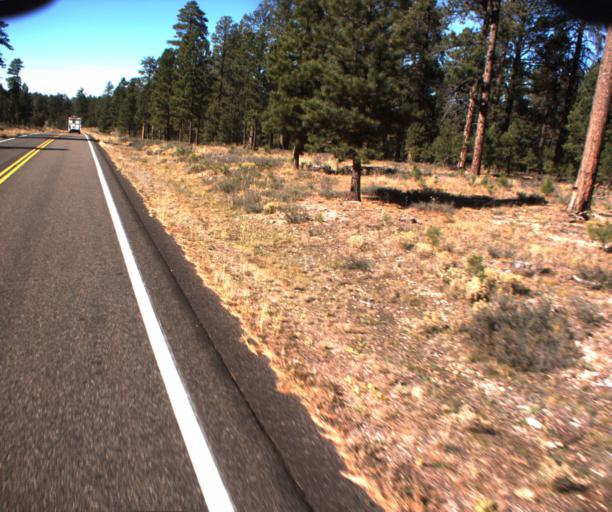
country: US
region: Arizona
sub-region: Coconino County
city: Fredonia
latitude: 36.6679
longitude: -112.2007
